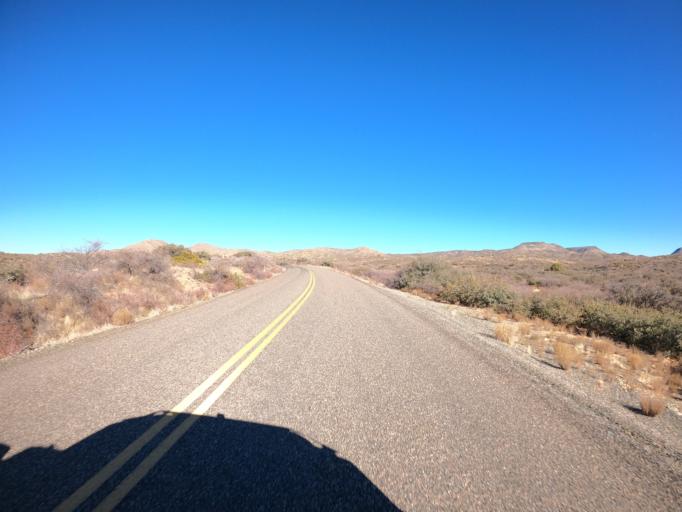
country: US
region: Arizona
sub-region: Yavapai County
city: Dewey-Humboldt
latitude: 34.5307
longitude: -112.0808
